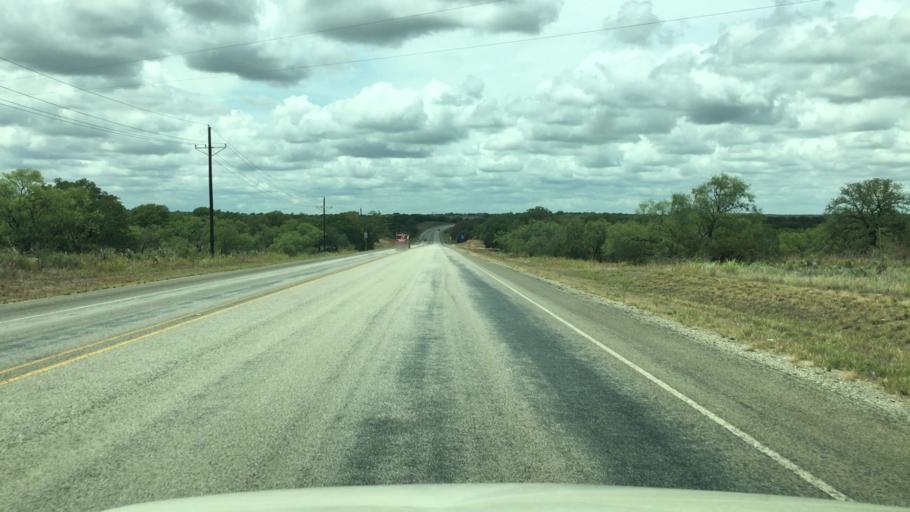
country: US
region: Texas
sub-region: McCulloch County
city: Brady
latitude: 31.0032
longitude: -99.1901
